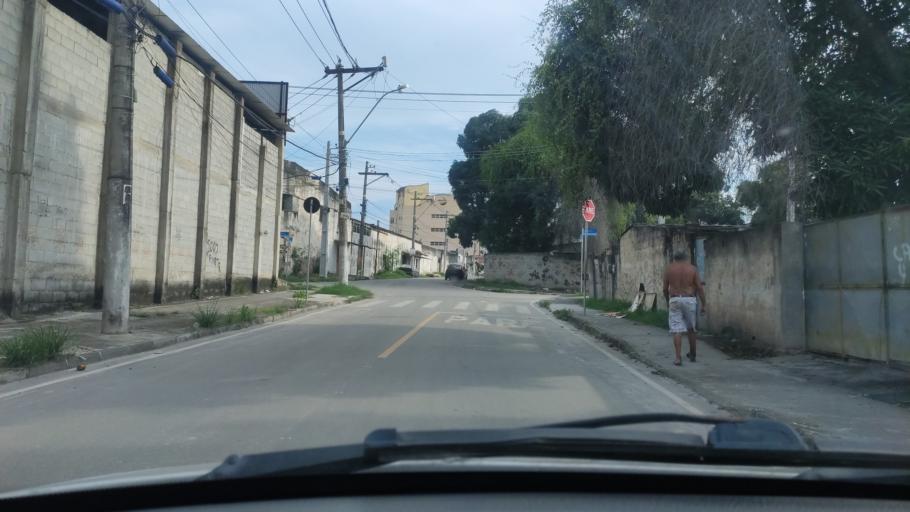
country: BR
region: Rio de Janeiro
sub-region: Itaborai
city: Itaborai
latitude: -22.7782
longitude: -42.9379
